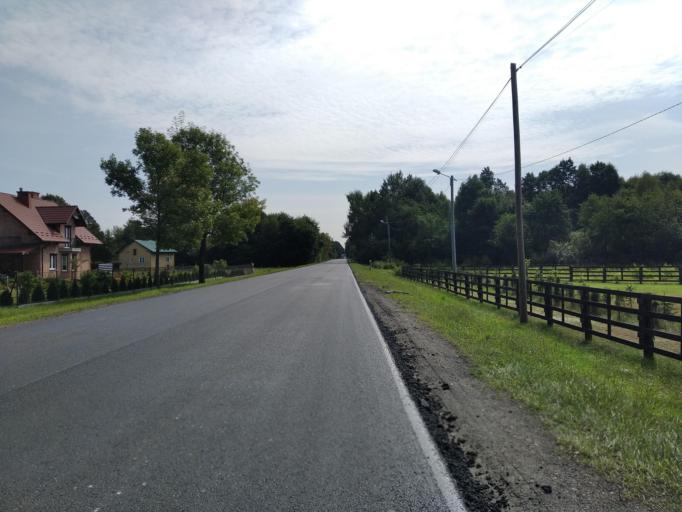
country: PL
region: Subcarpathian Voivodeship
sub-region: Powiat ropczycko-sedziszowski
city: Ostrow
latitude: 50.1564
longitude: 21.5568
